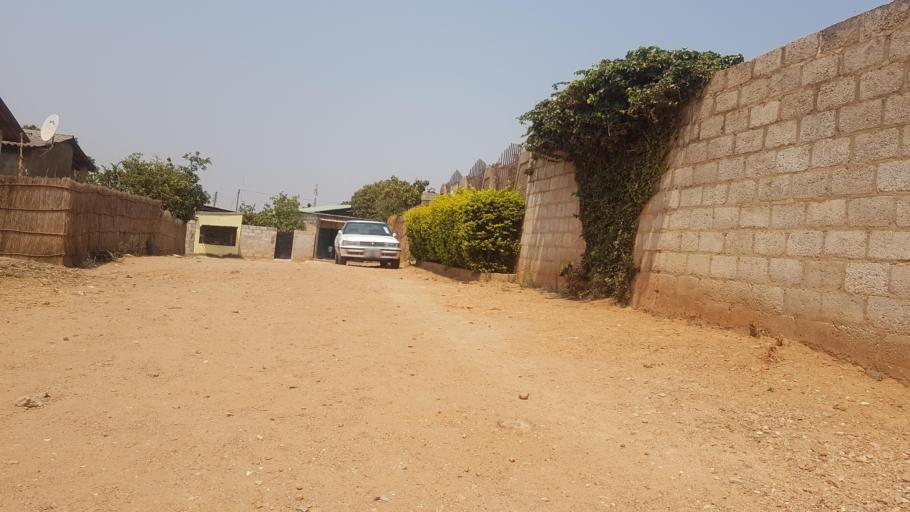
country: ZM
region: Lusaka
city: Lusaka
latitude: -15.4391
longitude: 28.3836
